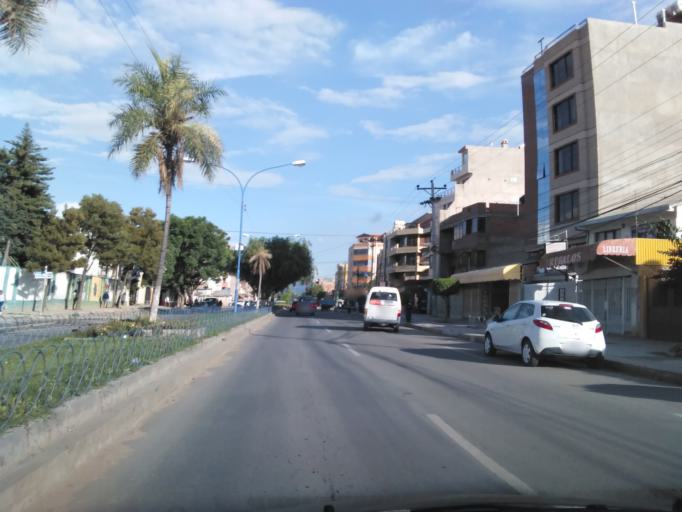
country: BO
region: Cochabamba
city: Cochabamba
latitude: -17.3539
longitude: -66.1886
